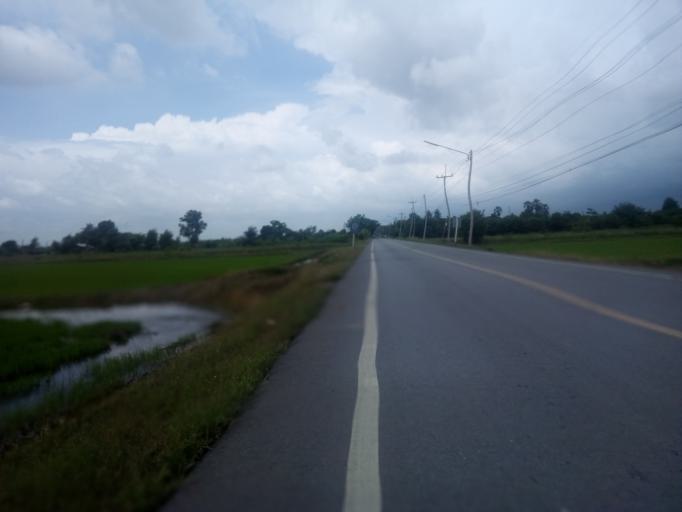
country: TH
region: Pathum Thani
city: Ban Lam Luk Ka
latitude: 13.9831
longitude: 100.8205
